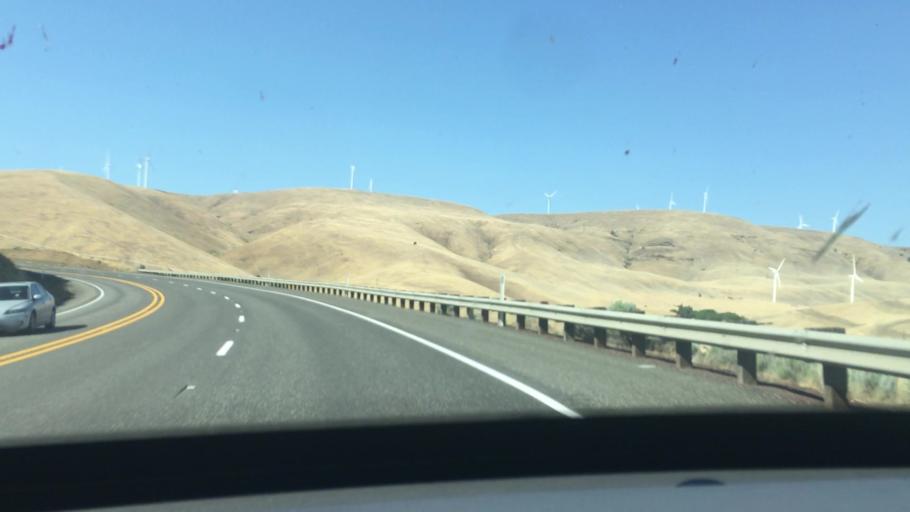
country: US
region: Washington
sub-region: Klickitat County
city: Goldendale
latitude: 45.7111
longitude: -120.8009
